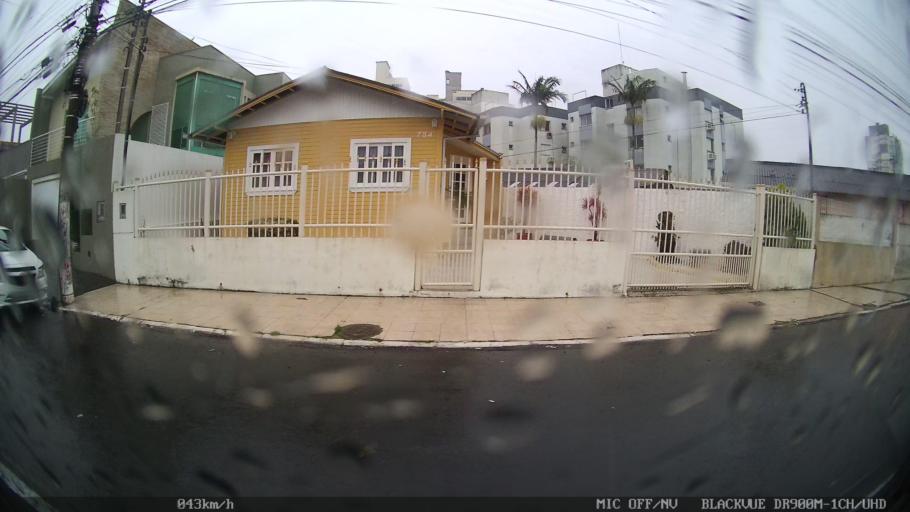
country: BR
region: Santa Catarina
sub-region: Itajai
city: Itajai
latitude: -26.9119
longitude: -48.6700
